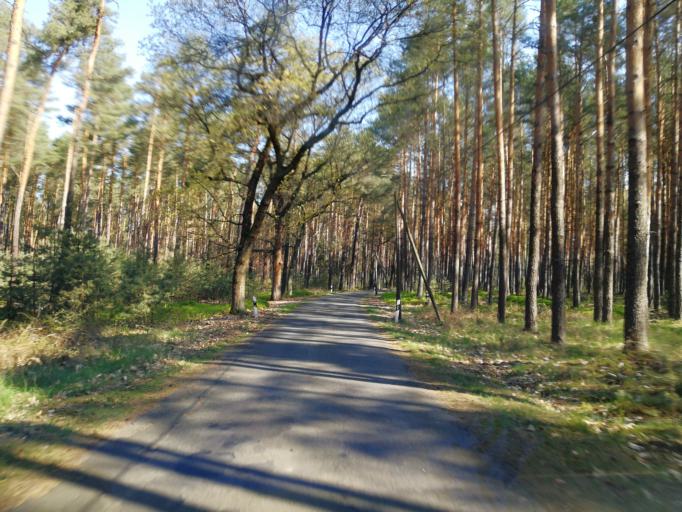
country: DE
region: Brandenburg
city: Bronkow
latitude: 51.6841
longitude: 13.8646
